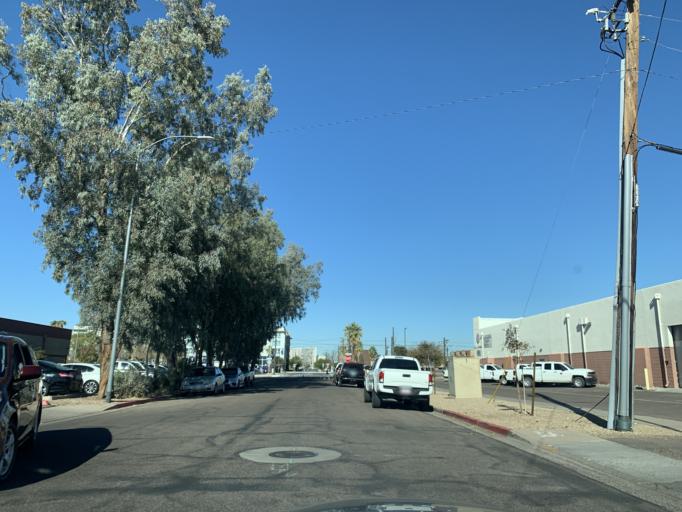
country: US
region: Arizona
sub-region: Maricopa County
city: Phoenix
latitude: 33.4463
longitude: -112.0590
